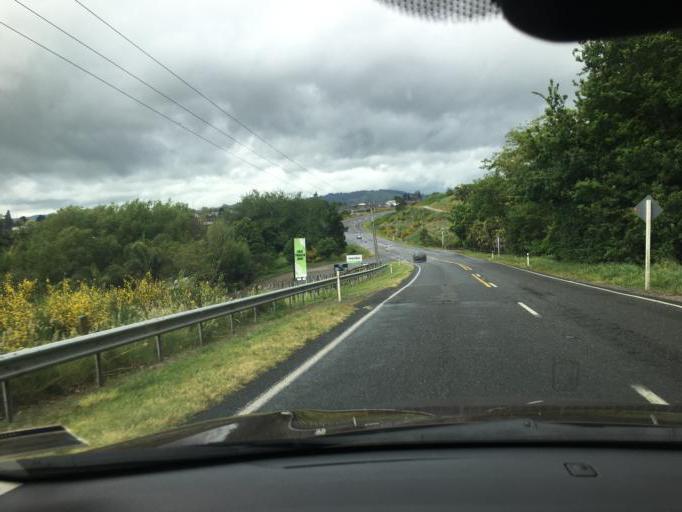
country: NZ
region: Waikato
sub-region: Waipa District
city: Cambridge
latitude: -37.9010
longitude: 175.4539
